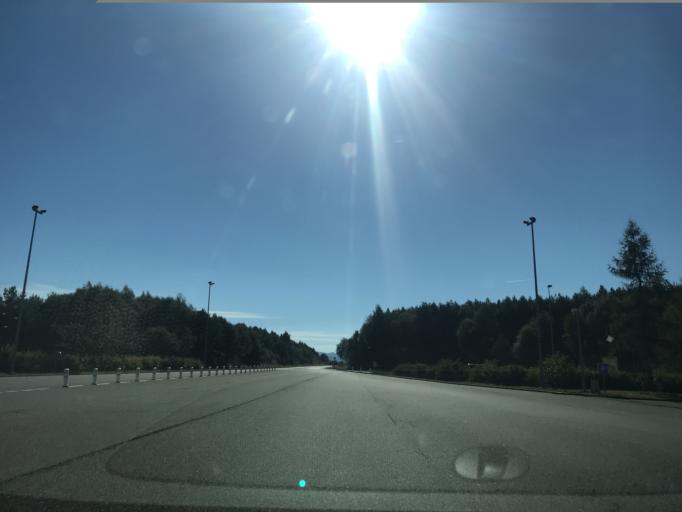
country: FR
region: Auvergne
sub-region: Departement du Puy-de-Dome
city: Saint-Sauves-d'Auvergne
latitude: 45.6661
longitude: 2.6825
